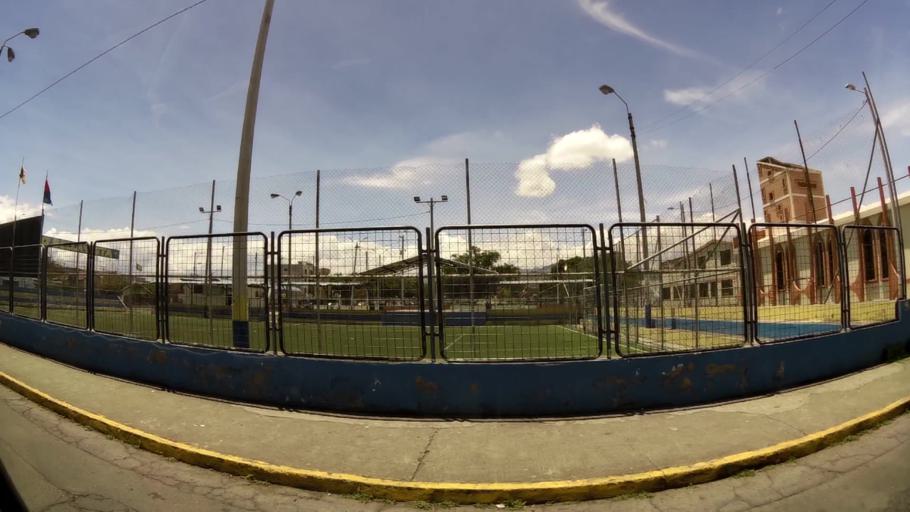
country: EC
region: Chimborazo
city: Riobamba
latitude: -1.6734
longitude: -78.6380
